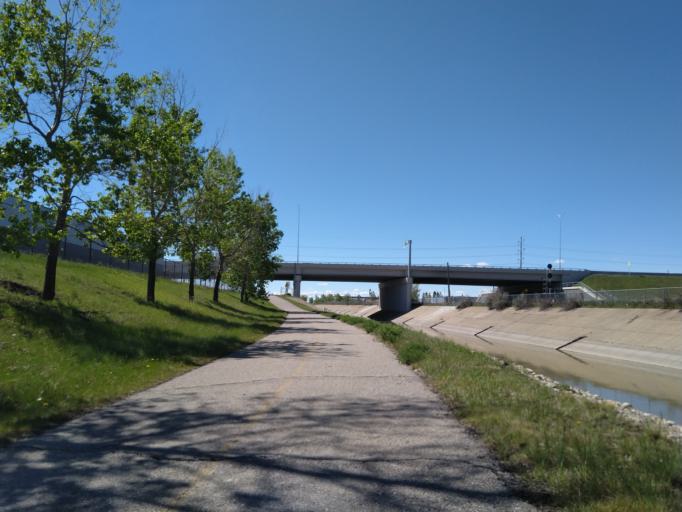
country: CA
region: Alberta
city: Calgary
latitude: 50.9807
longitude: -113.9933
